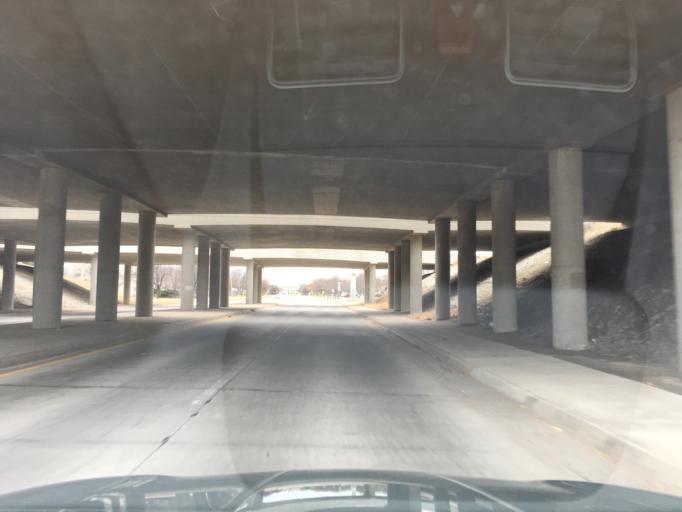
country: US
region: Kansas
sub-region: Sedgwick County
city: Wichita
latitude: 37.6797
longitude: -97.3082
